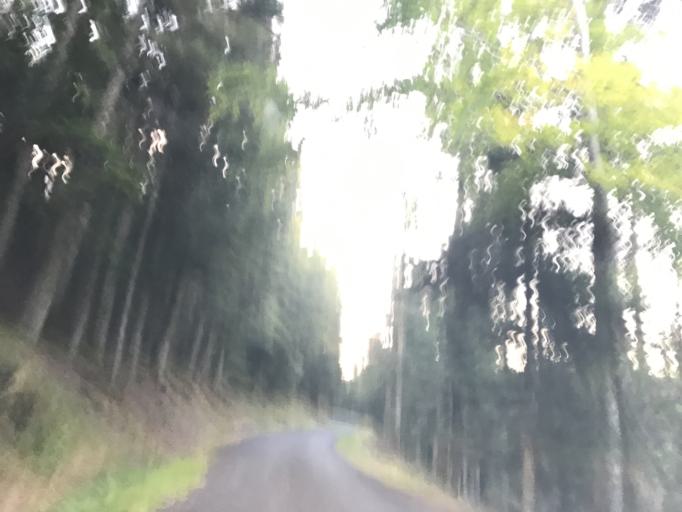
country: FR
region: Rhone-Alpes
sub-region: Departement de la Loire
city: Noiretable
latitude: 45.7614
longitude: 3.7298
